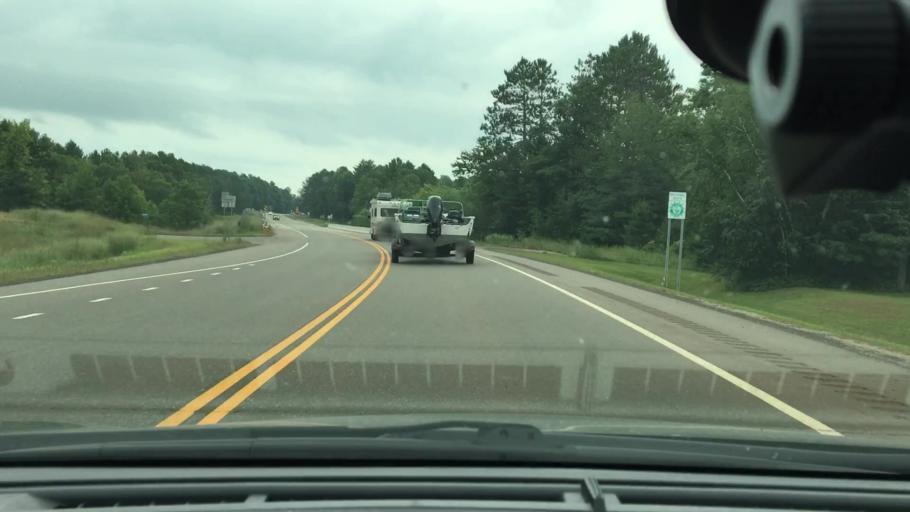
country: US
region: Minnesota
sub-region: Crow Wing County
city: Crosby
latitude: 46.5451
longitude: -93.9575
